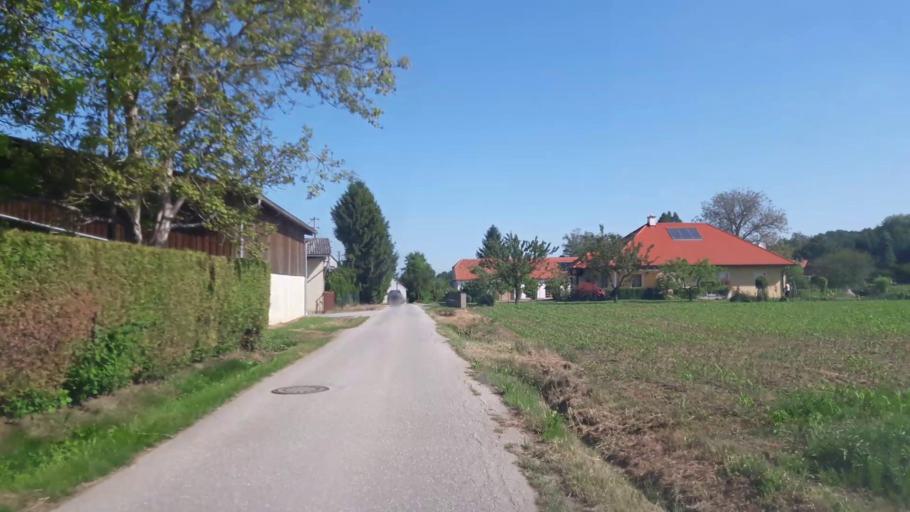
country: AT
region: Burgenland
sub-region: Politischer Bezirk Jennersdorf
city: Deutsch Kaltenbrunn
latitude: 47.0896
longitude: 16.1091
